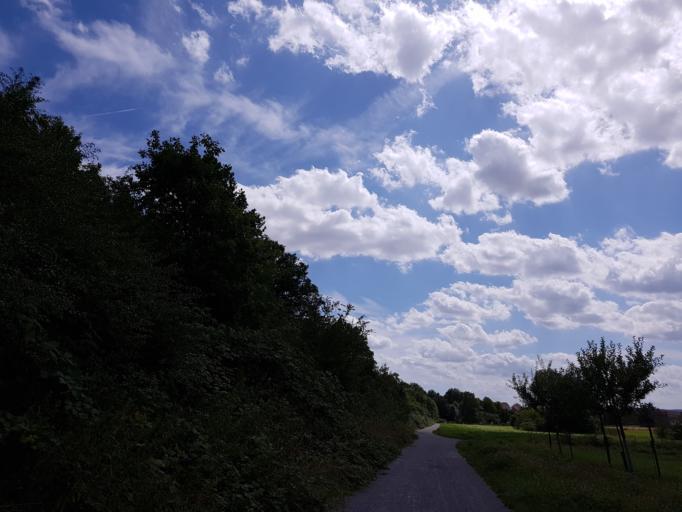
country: DE
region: Hesse
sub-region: Regierungsbezirk Giessen
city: Langgons
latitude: 50.5076
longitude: 8.6667
